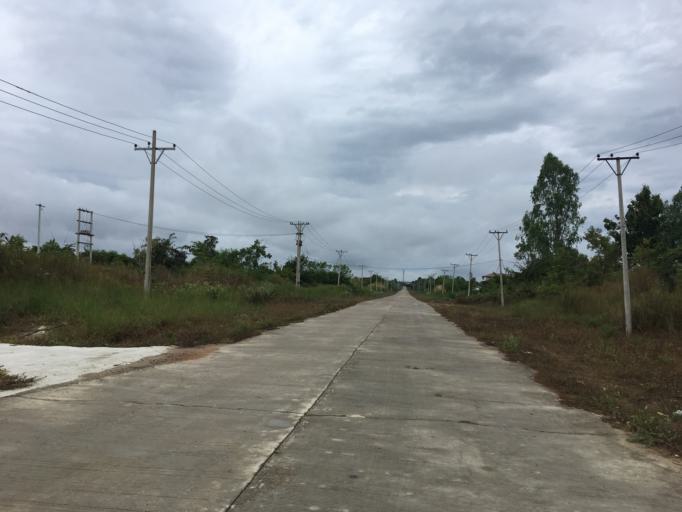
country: MM
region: Mandalay
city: Nay Pyi Taw
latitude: 19.6966
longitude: 96.1209
